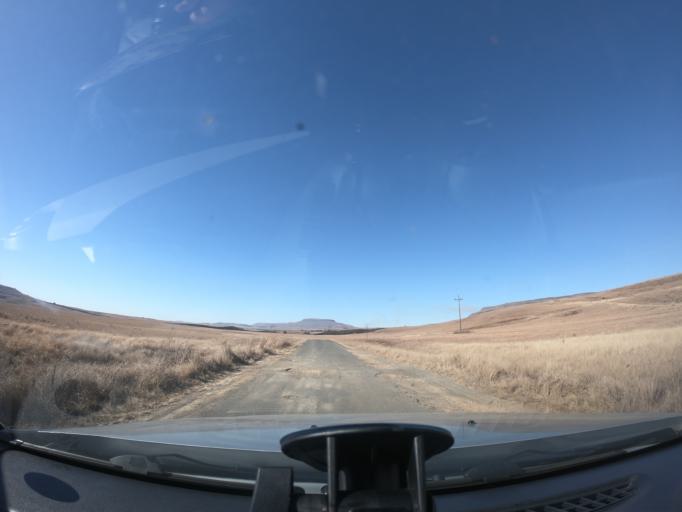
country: ZA
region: KwaZulu-Natal
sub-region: uMgungundlovu District Municipality
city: Impendle
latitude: -29.3862
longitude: 29.7208
